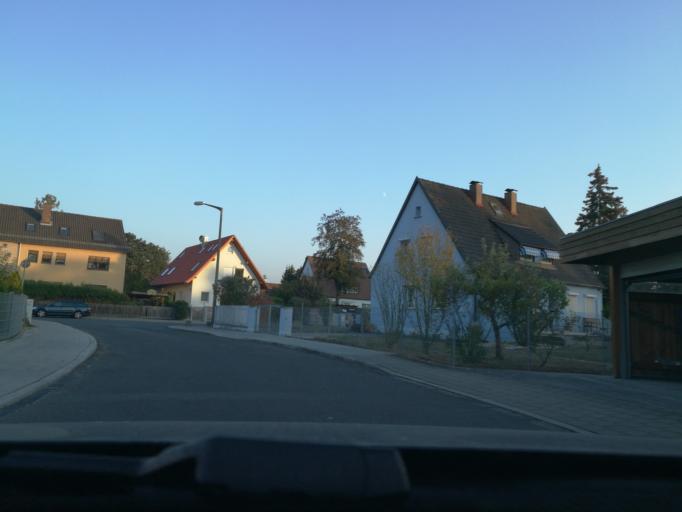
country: DE
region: Bavaria
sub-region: Regierungsbezirk Mittelfranken
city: Furth
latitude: 49.4892
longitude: 10.9941
